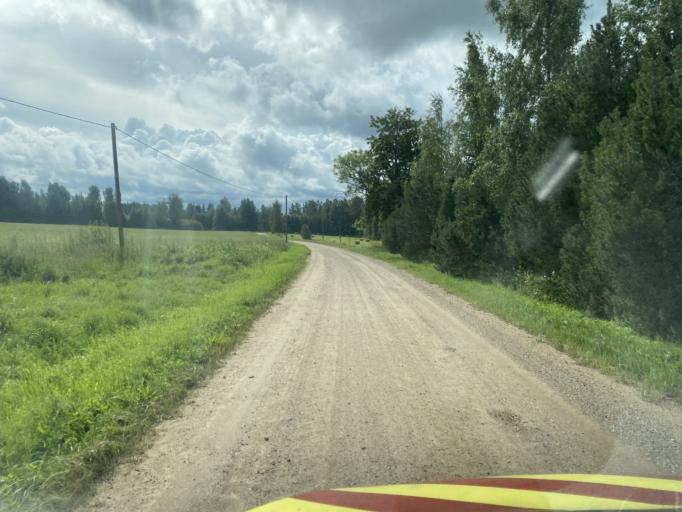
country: EE
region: Viljandimaa
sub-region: Karksi vald
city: Karksi-Nuia
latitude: 58.0631
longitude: 25.5315
